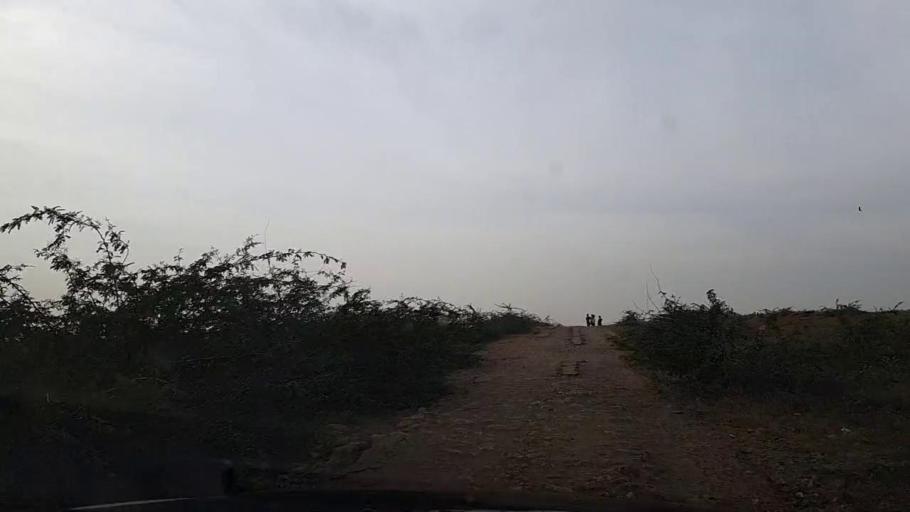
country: PK
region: Sindh
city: Gharo
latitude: 24.7928
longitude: 67.5448
